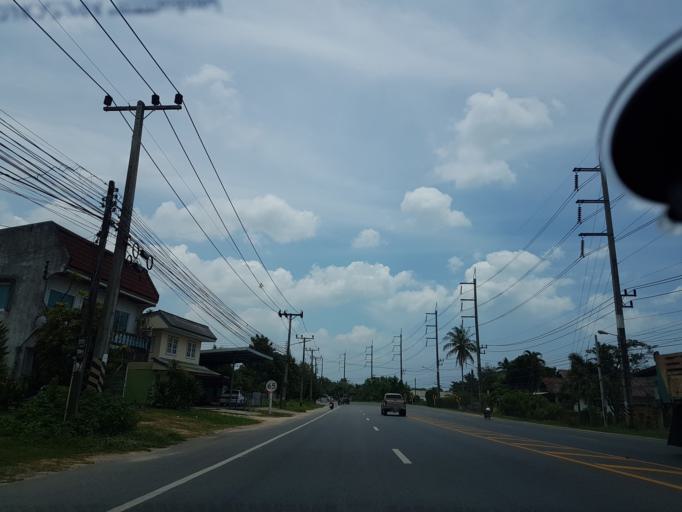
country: TH
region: Songkhla
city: Songkhla
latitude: 7.1241
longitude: 100.6321
